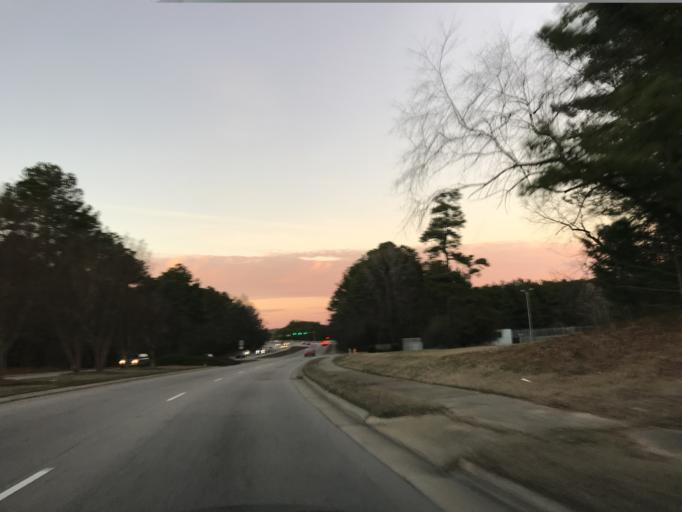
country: US
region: North Carolina
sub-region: Wake County
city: Raleigh
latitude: 35.7727
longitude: -78.5603
